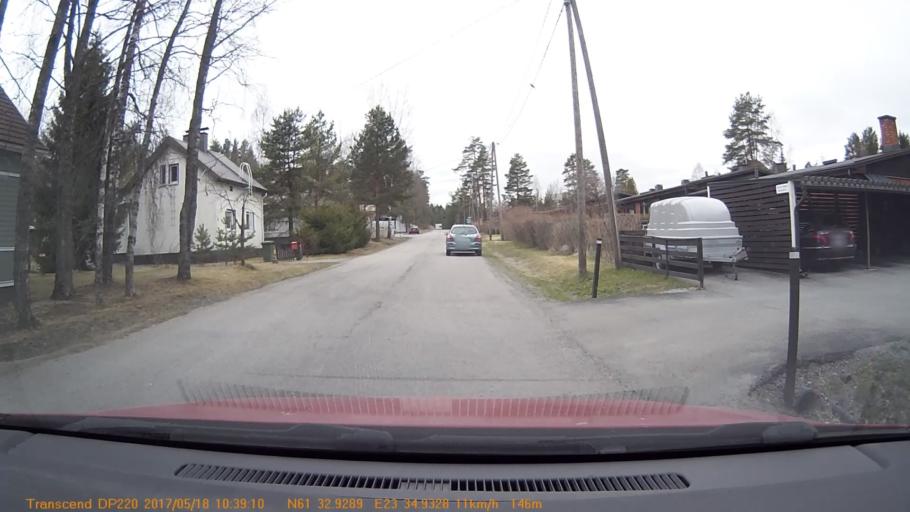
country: FI
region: Pirkanmaa
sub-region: Tampere
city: Yloejaervi
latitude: 61.5488
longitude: 23.5822
